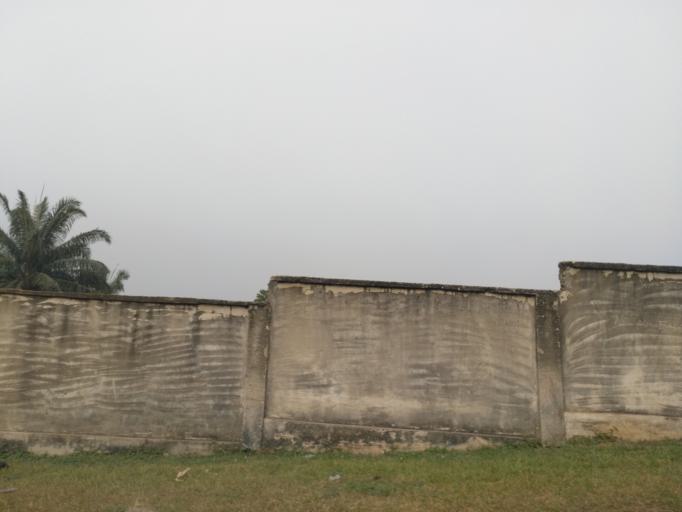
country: GH
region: Ashanti
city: Kumasi
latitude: 6.6568
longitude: -1.6229
